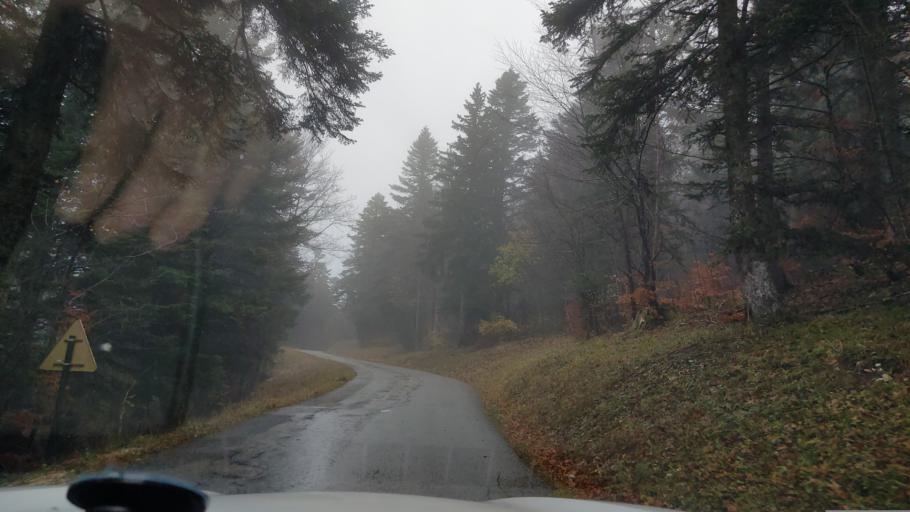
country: FR
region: Rhone-Alpes
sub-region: Departement de la Savoie
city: Le Bourget-du-Lac
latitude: 45.6588
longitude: 5.8162
